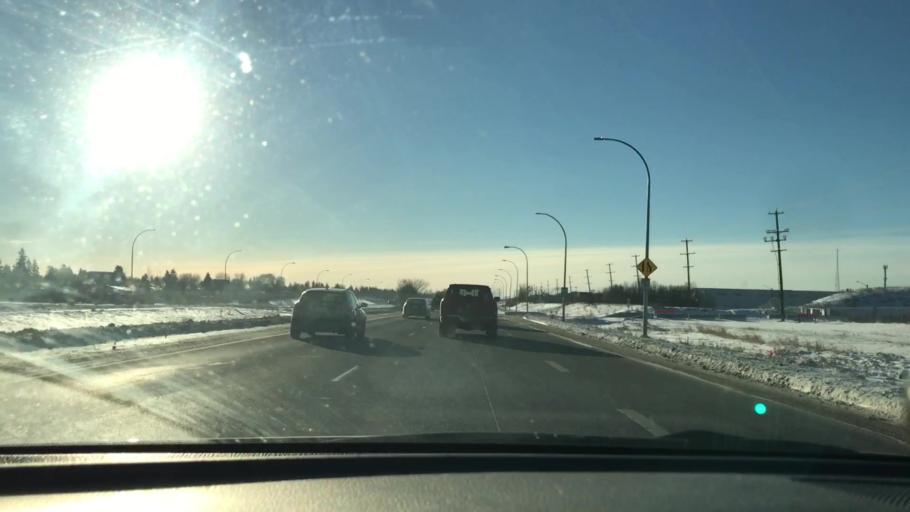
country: CA
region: Alberta
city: Edmonton
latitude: 53.4812
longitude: -113.4671
